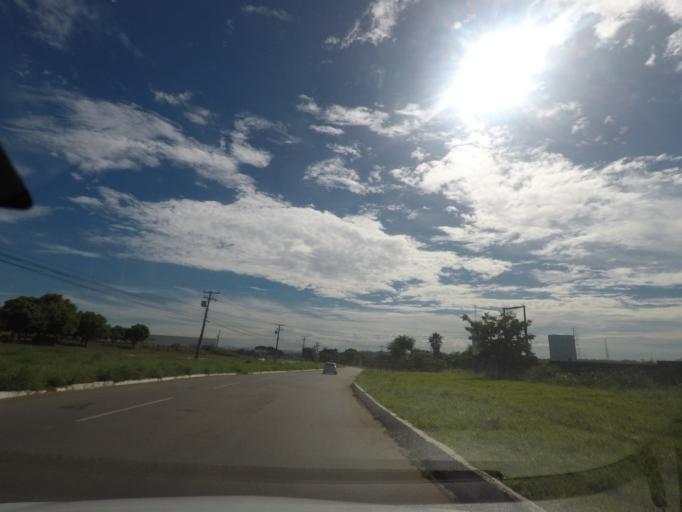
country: BR
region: Goias
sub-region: Aparecida De Goiania
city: Aparecida de Goiania
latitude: -16.8010
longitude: -49.2587
